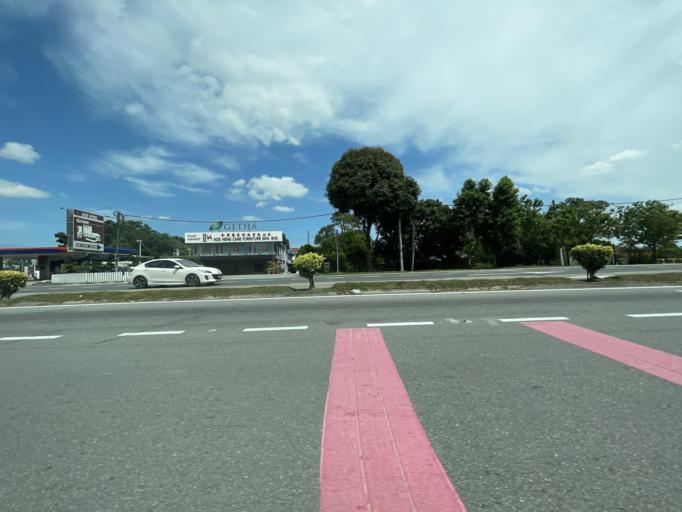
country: MY
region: Melaka
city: Batu Berendam
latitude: 2.2544
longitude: 102.2226
